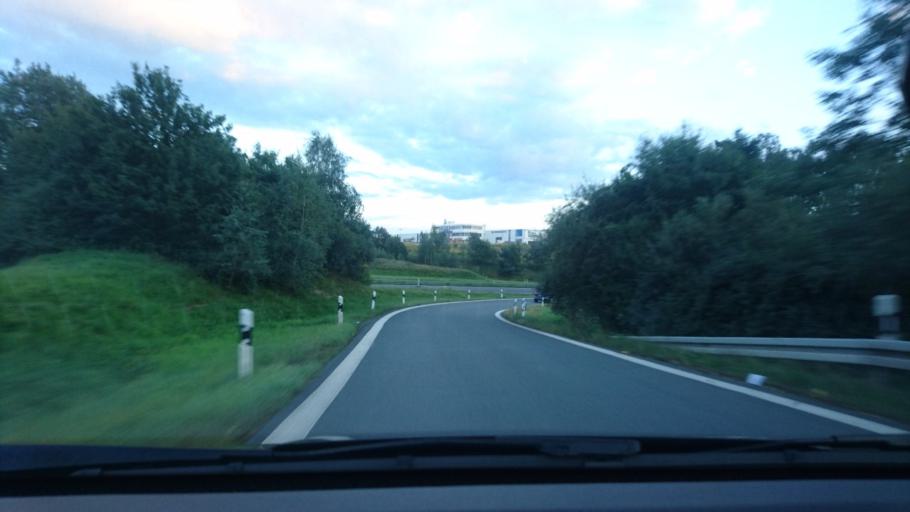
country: DE
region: Saxony
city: Treuen
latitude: 50.5529
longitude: 12.2748
